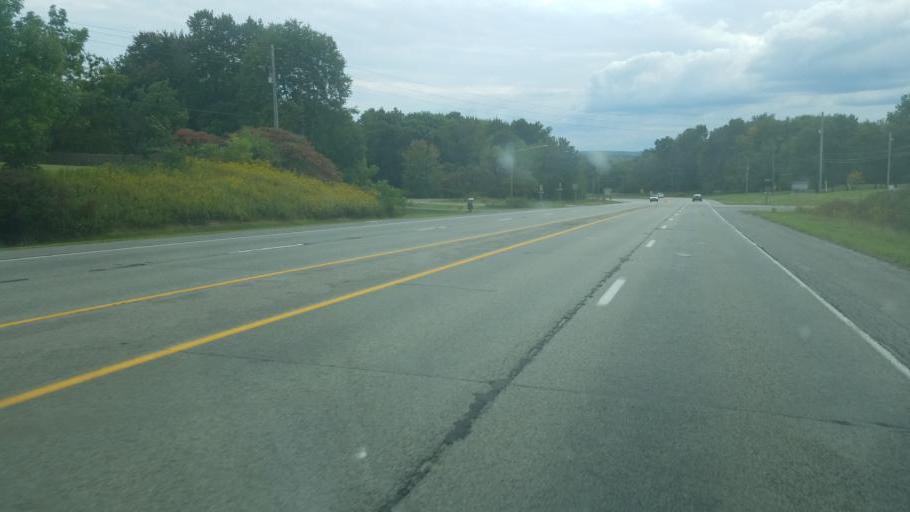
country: US
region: Pennsylvania
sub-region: Mercer County
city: Reynolds Heights
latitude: 41.3021
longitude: -80.4207
